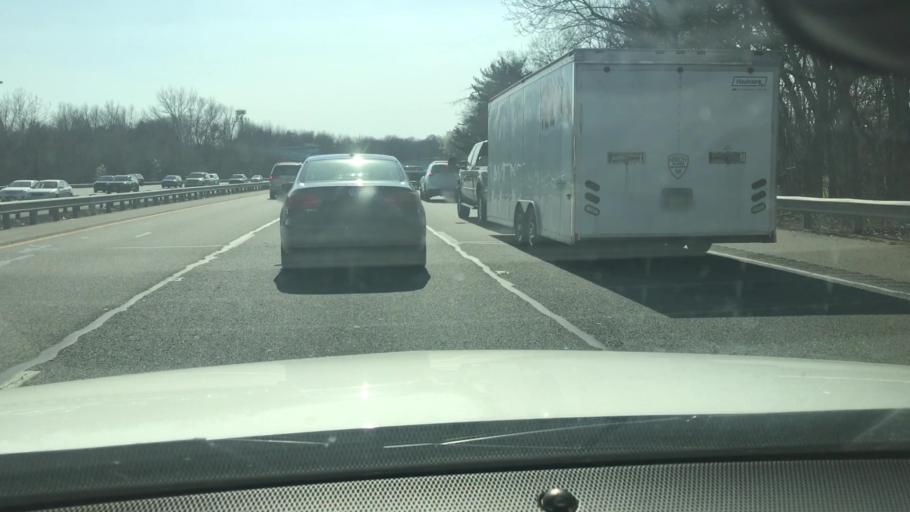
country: US
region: New Jersey
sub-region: Camden County
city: Lawnside
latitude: 39.8727
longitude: -75.0215
